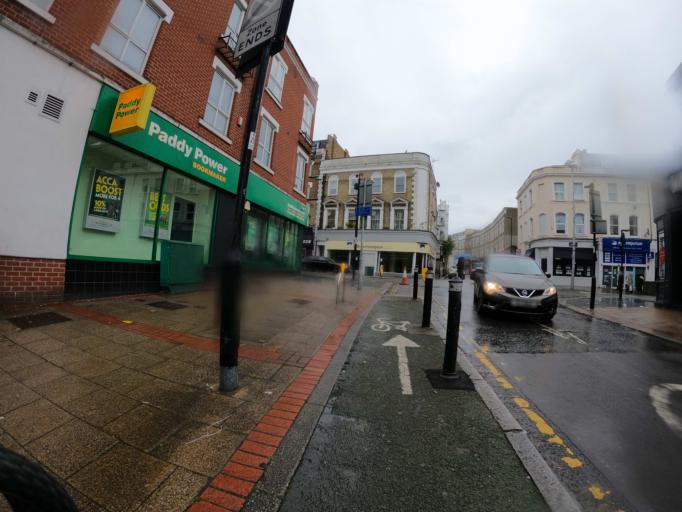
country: GB
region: England
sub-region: Greater London
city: Acton
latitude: 51.5070
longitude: -0.2713
